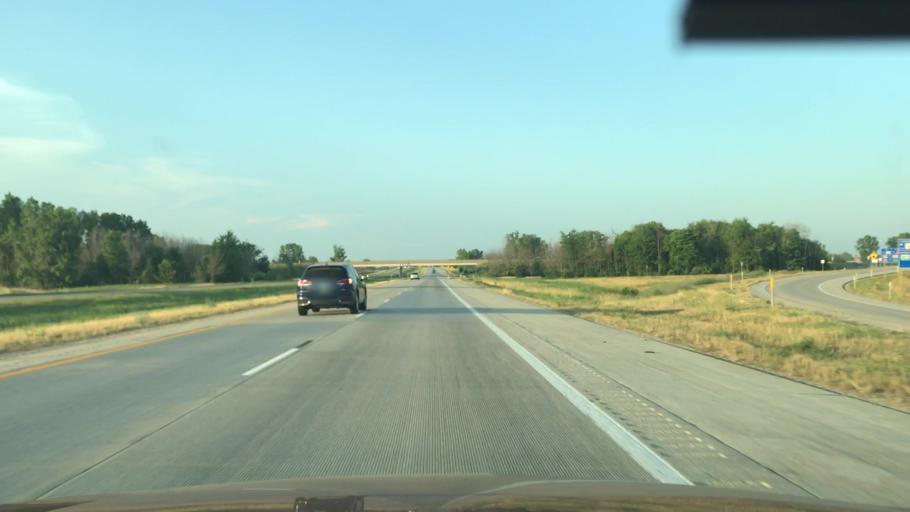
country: US
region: Michigan
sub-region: Ottawa County
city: Holland
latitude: 42.7412
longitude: -86.0756
